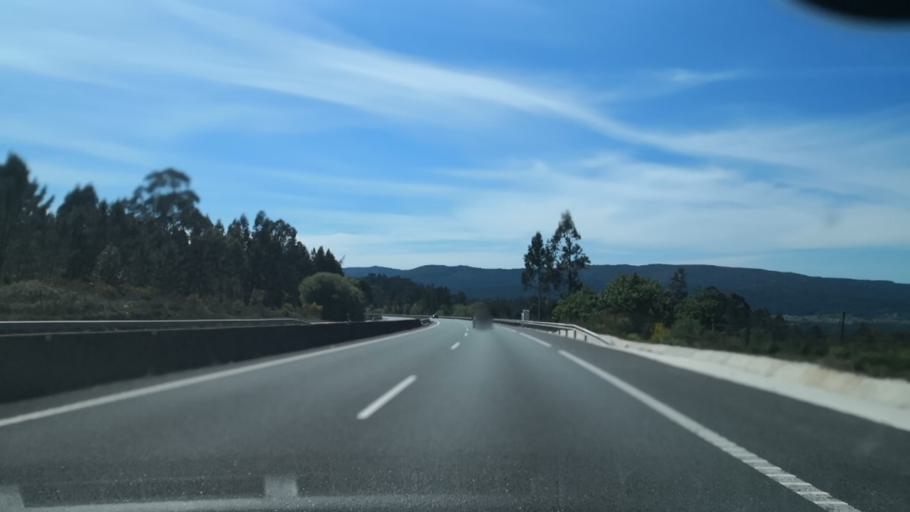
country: ES
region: Galicia
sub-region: Provincia da Coruna
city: Padron
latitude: 42.8067
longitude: -8.6125
